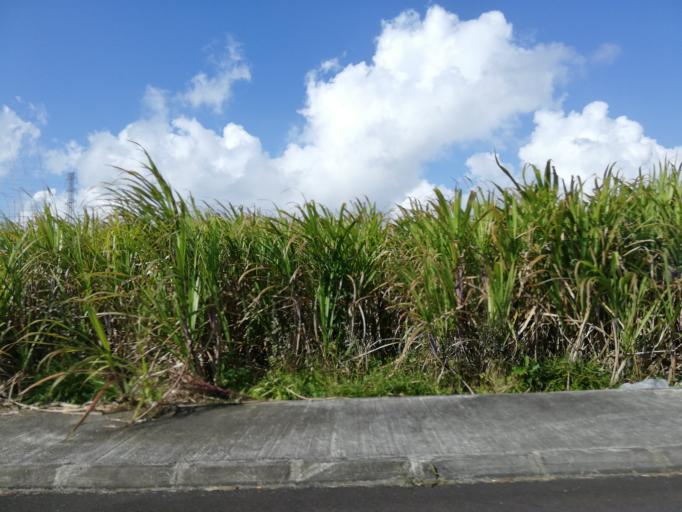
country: MU
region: Pamplemousses
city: Creve Coeur
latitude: -20.2071
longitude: 57.5676
